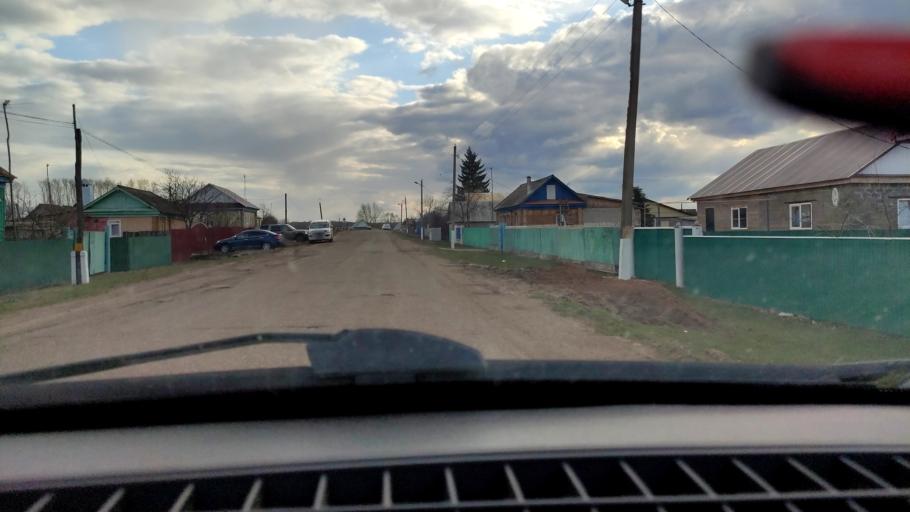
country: RU
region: Bashkortostan
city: Karmaskaly
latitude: 54.3340
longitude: 55.9960
